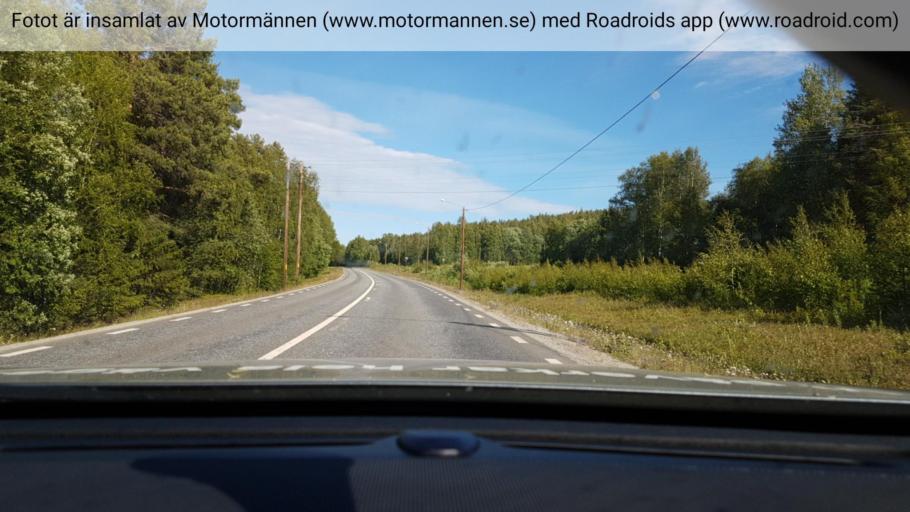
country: SE
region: Vaesterbotten
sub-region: Lycksele Kommun
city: Soderfors
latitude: 64.7040
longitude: 18.3301
